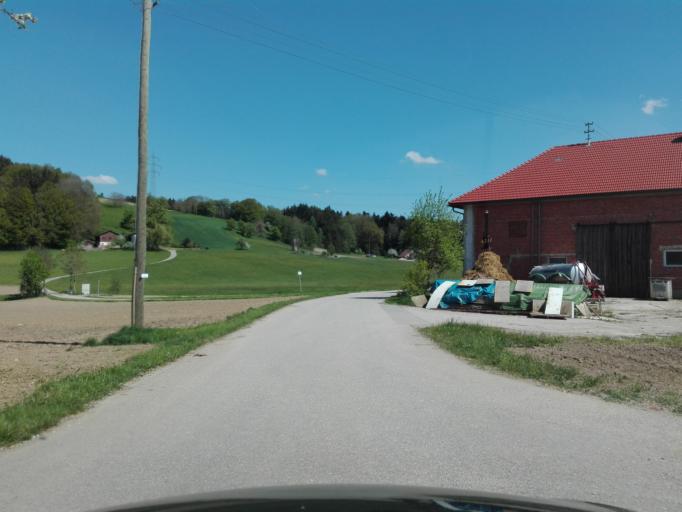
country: AT
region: Upper Austria
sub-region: Politischer Bezirk Grieskirchen
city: Bad Schallerbach
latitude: 48.3436
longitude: 13.8940
